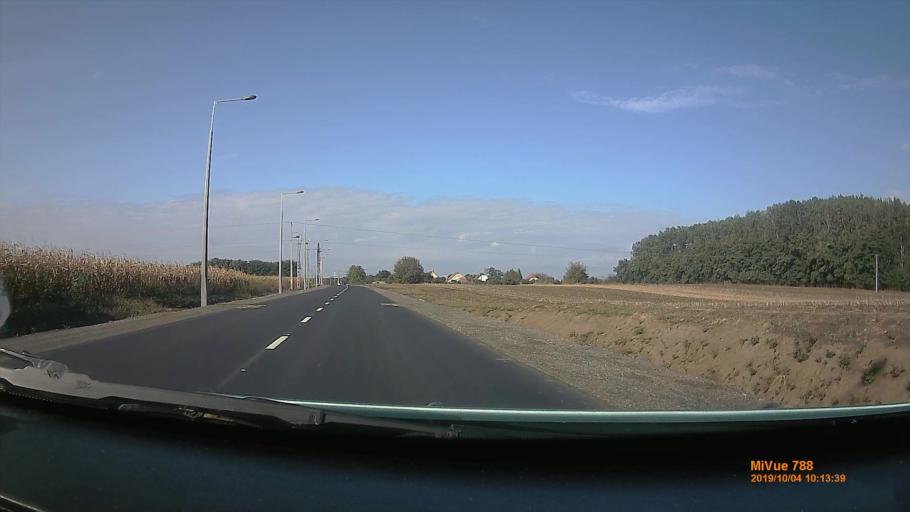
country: HU
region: Szabolcs-Szatmar-Bereg
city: Nyiregyhaza
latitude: 47.9419
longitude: 21.6801
